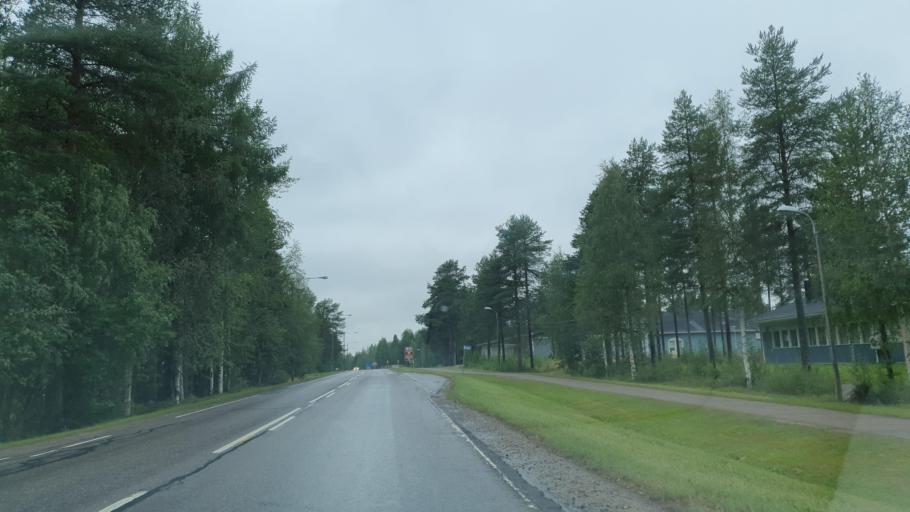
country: FI
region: Lapland
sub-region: Itae-Lappi
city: Kemijaervi
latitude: 66.7190
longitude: 27.3797
